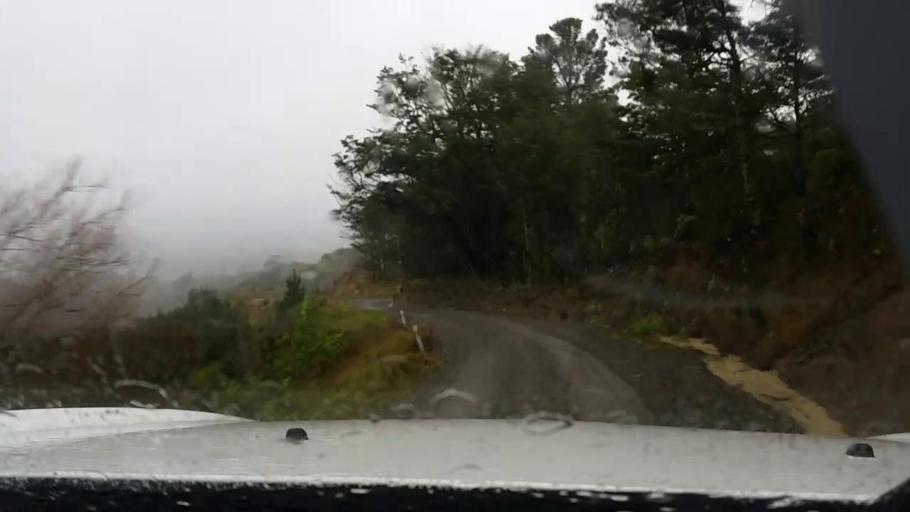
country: NZ
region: Wellington
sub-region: Masterton District
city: Masterton
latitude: -41.2022
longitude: 175.8119
